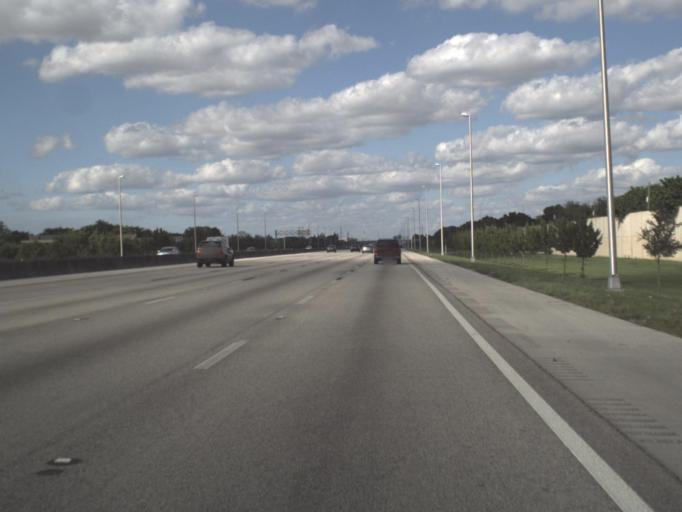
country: US
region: Florida
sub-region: Broward County
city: Lauderhill
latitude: 26.1532
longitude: -80.2194
